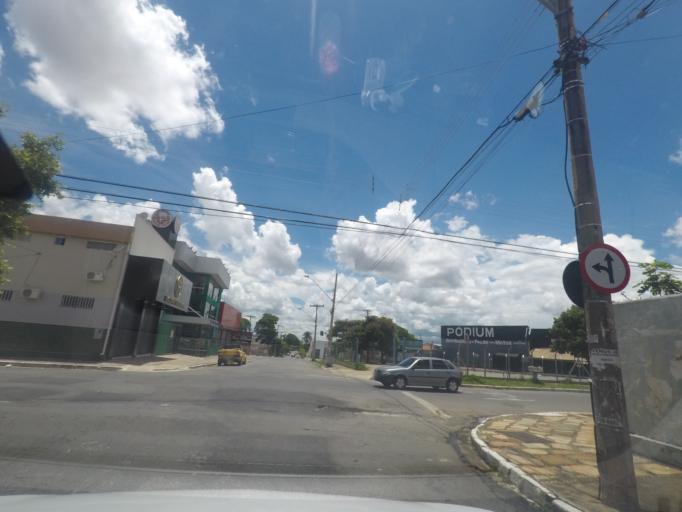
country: BR
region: Goias
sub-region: Goiania
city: Goiania
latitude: -16.6673
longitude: -49.2881
